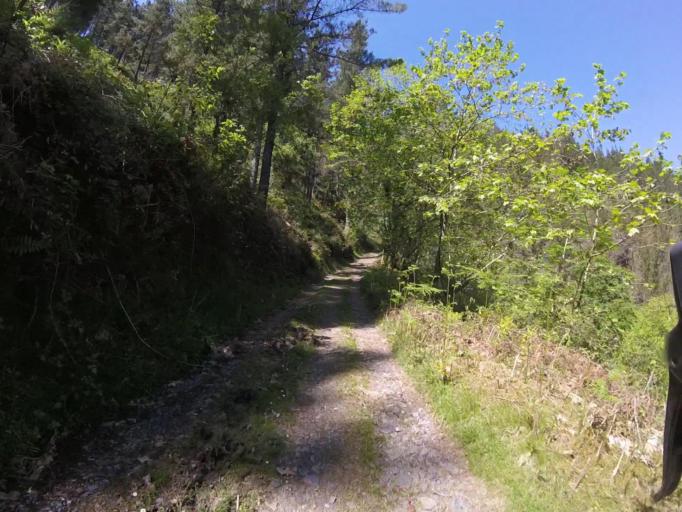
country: ES
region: Navarre
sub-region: Provincia de Navarra
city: Lesaka
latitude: 43.2480
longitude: -1.7557
